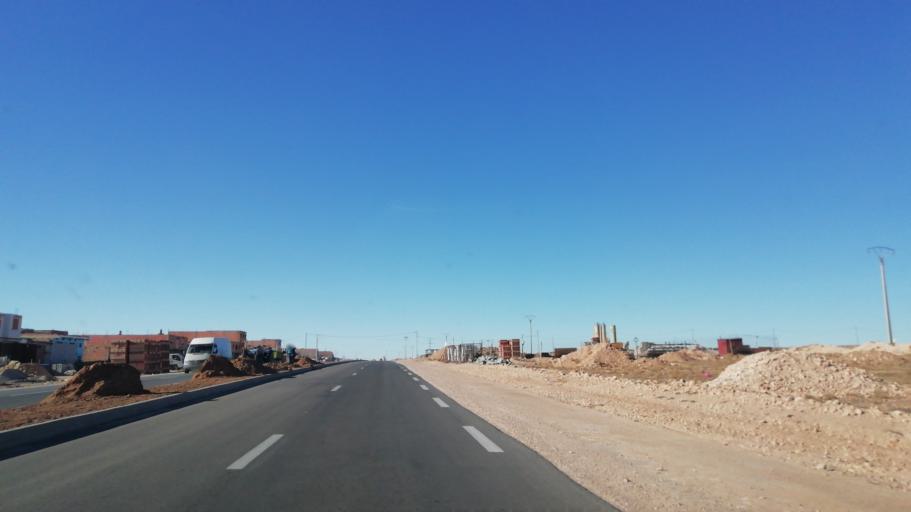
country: DZ
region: Tlemcen
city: Sebdou
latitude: 34.2166
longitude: -1.2460
